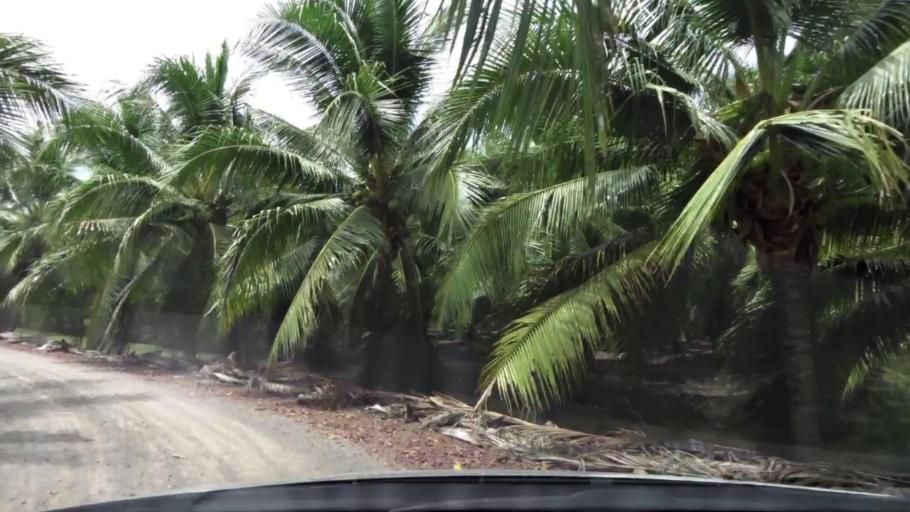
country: TH
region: Ratchaburi
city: Damnoen Saduak
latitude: 13.5167
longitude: 100.0149
